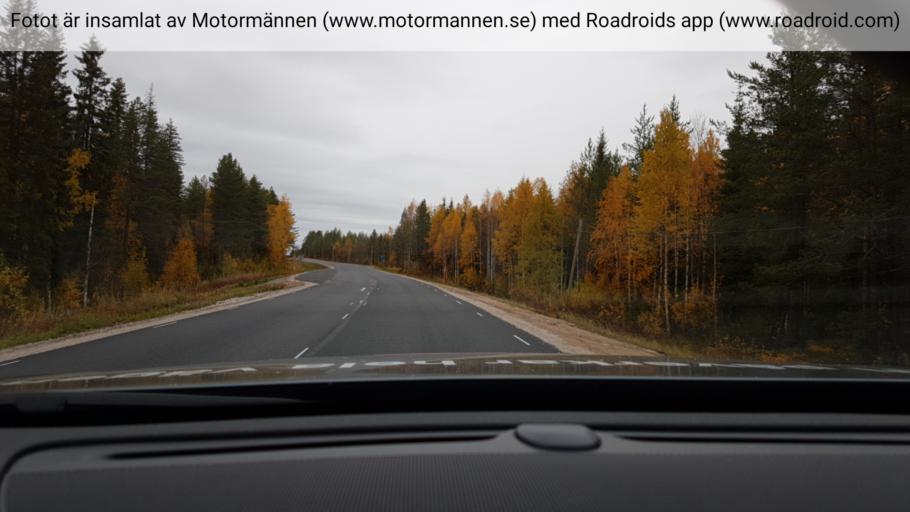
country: SE
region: Norrbotten
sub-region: Overkalix Kommun
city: OEverkalix
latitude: 66.3732
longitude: 22.8422
